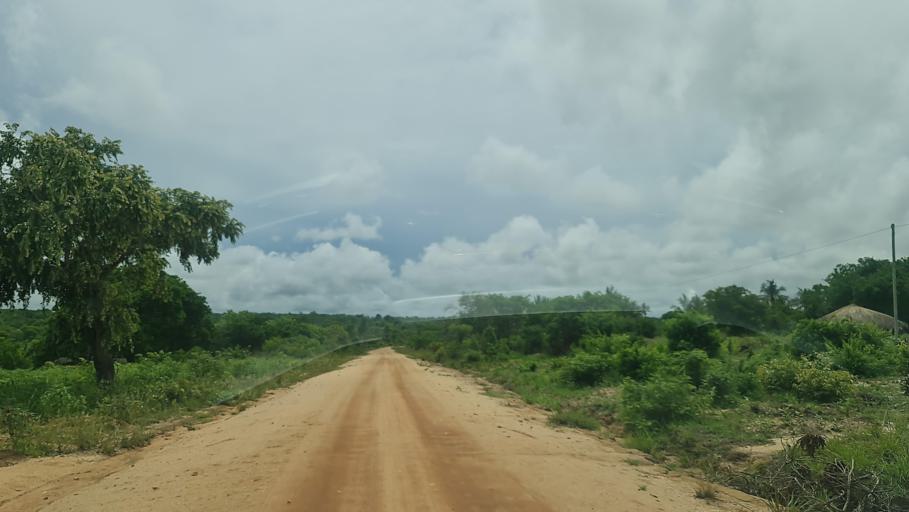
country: MZ
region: Zambezia
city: Quelimane
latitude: -17.2677
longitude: 37.2484
